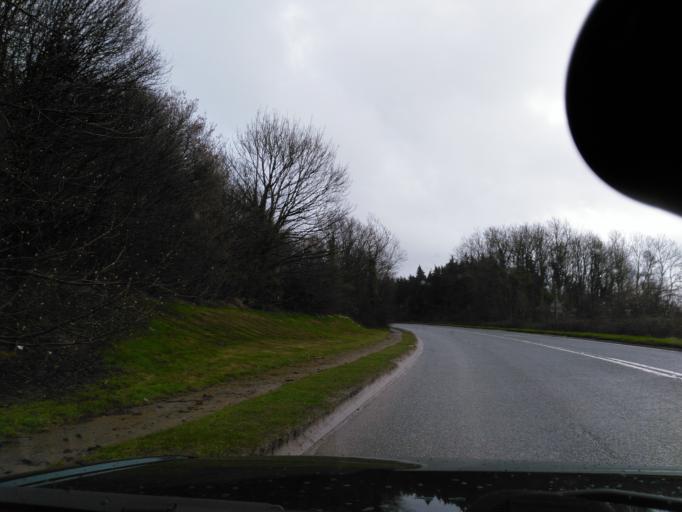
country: GB
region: England
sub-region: Somerset
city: Evercreech
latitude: 51.1908
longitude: -2.4398
